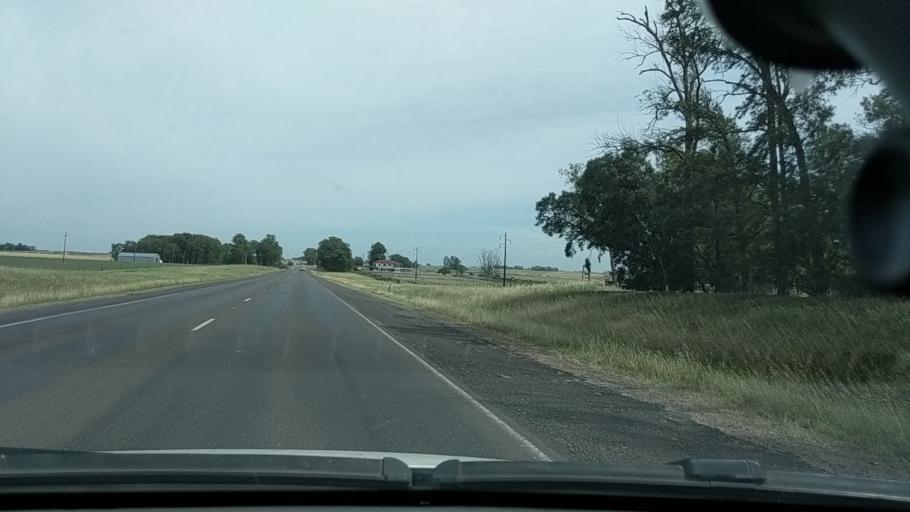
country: UY
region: Durazno
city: Durazno
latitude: -33.4936
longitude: -56.4304
